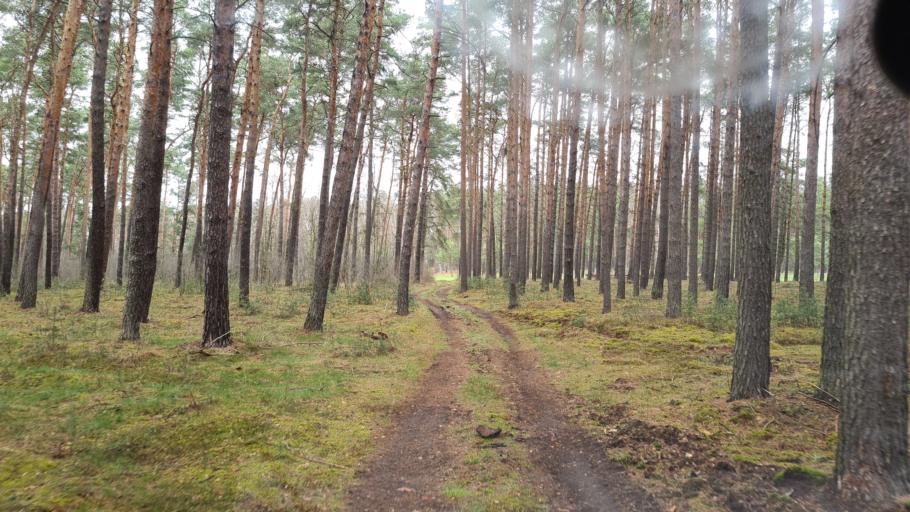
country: DE
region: Brandenburg
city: Schonewalde
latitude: 51.6468
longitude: 13.6268
